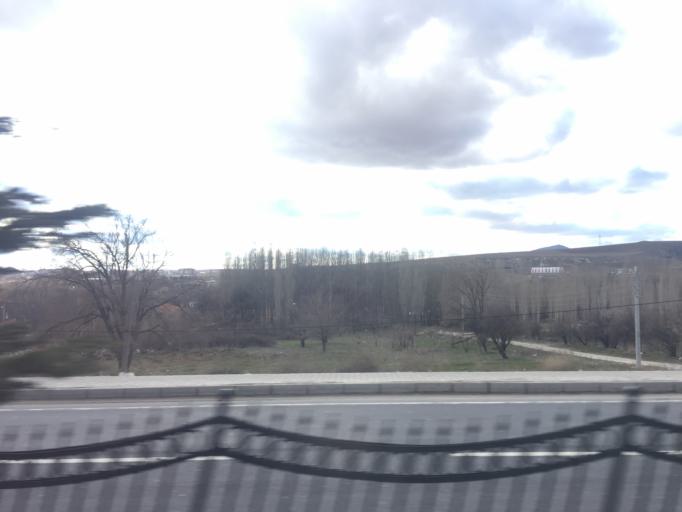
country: TR
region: Kirsehir
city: Kirsehir
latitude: 39.1679
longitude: 34.1517
